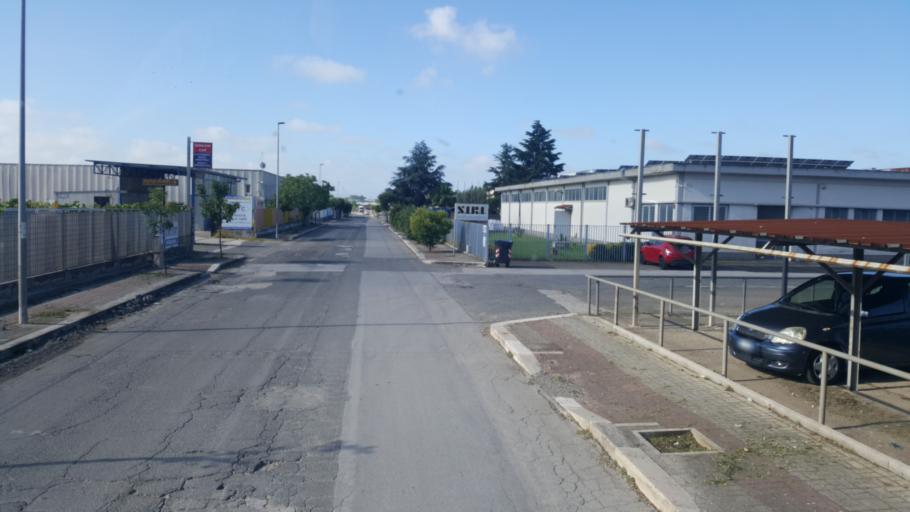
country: IT
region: Latium
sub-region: Provincia di Latina
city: Aprilia
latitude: 41.5751
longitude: 12.6466
